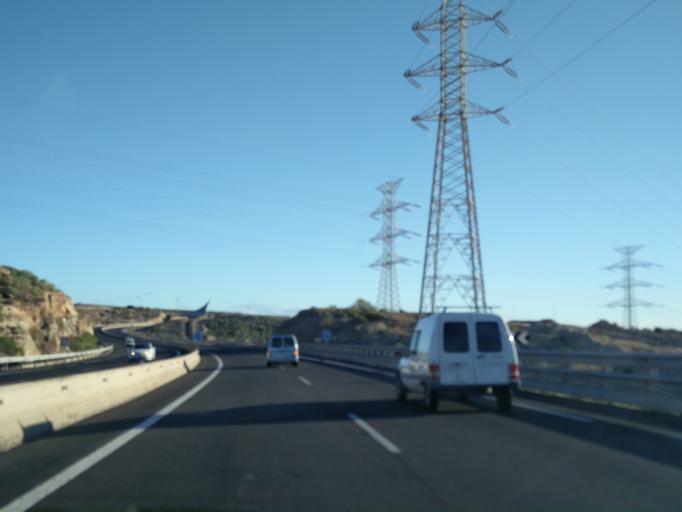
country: ES
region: Canary Islands
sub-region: Provincia de Santa Cruz de Tenerife
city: San Isidro
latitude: 28.0879
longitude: -16.5097
